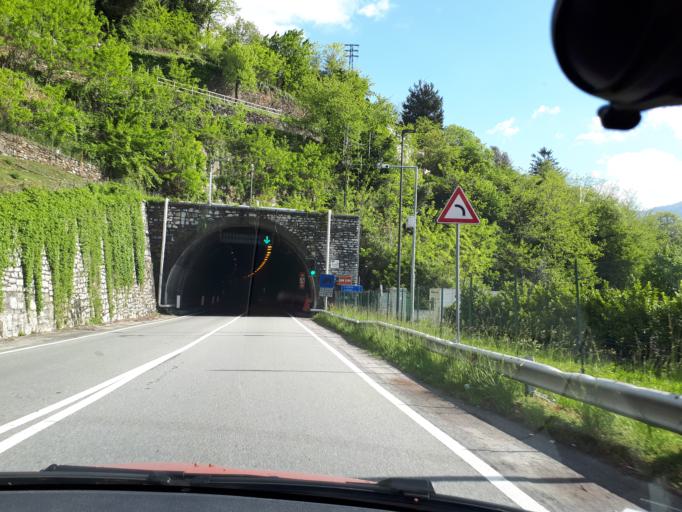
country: IT
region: Lombardy
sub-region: Provincia di Como
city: San Siro
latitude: 46.0719
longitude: 9.2763
